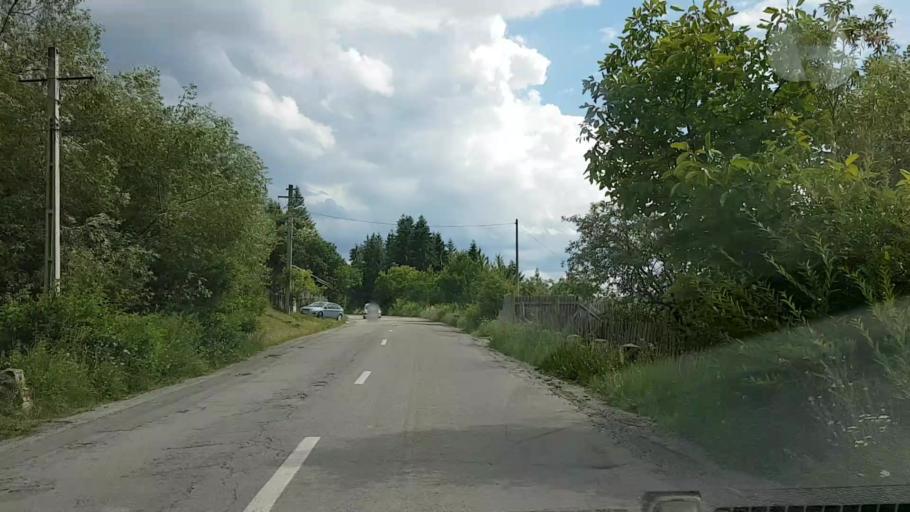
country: RO
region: Neamt
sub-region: Comuna Hangu
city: Hangu
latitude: 47.0562
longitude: 26.0376
